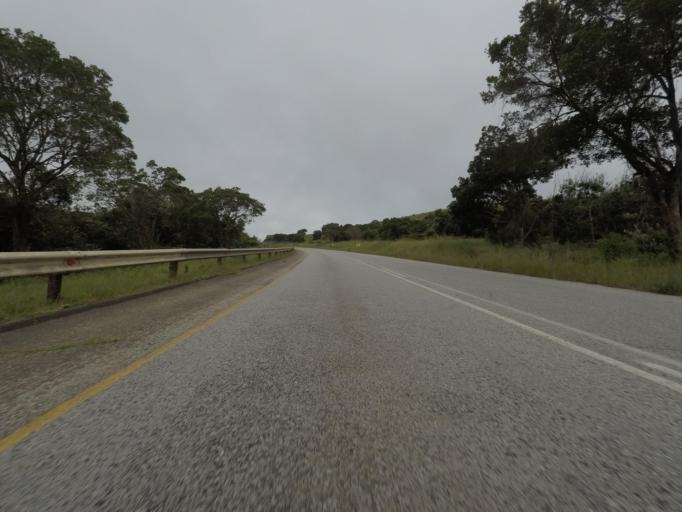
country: ZA
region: Eastern Cape
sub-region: Cacadu District Municipality
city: Port Alfred
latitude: -33.6138
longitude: 26.8036
